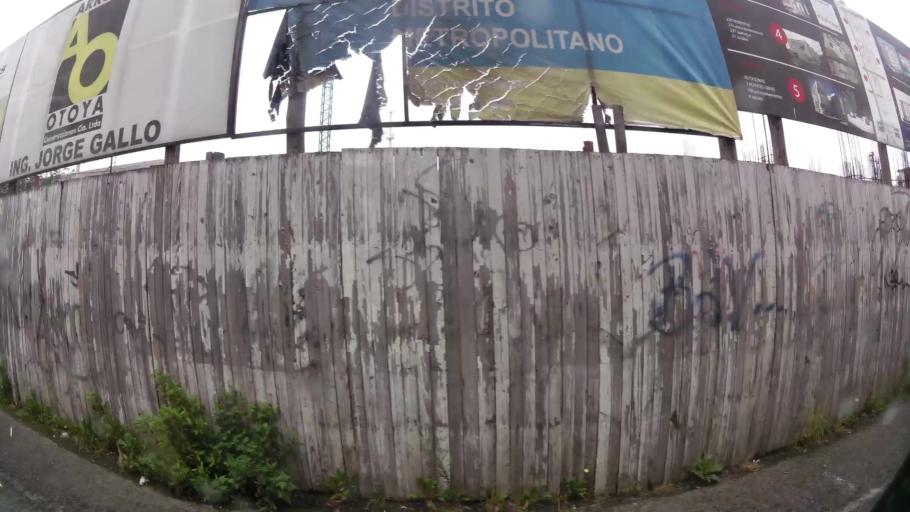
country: EC
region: Pichincha
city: Quito
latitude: -0.2084
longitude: -78.5017
